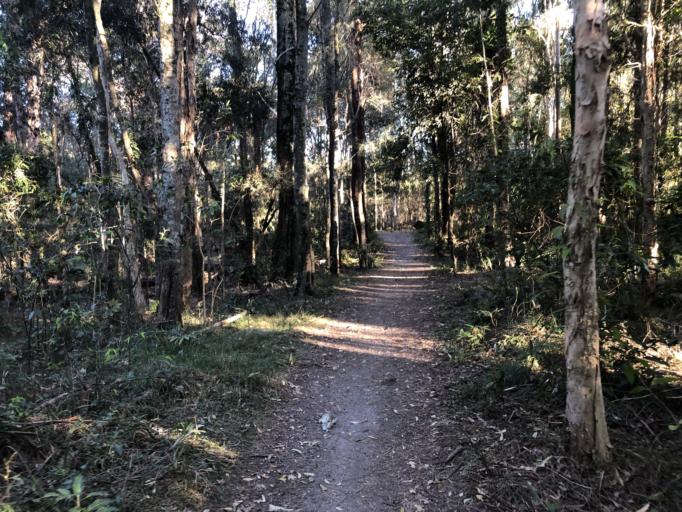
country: AU
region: New South Wales
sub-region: Coffs Harbour
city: Coffs Harbour
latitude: -30.2878
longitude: 153.1269
